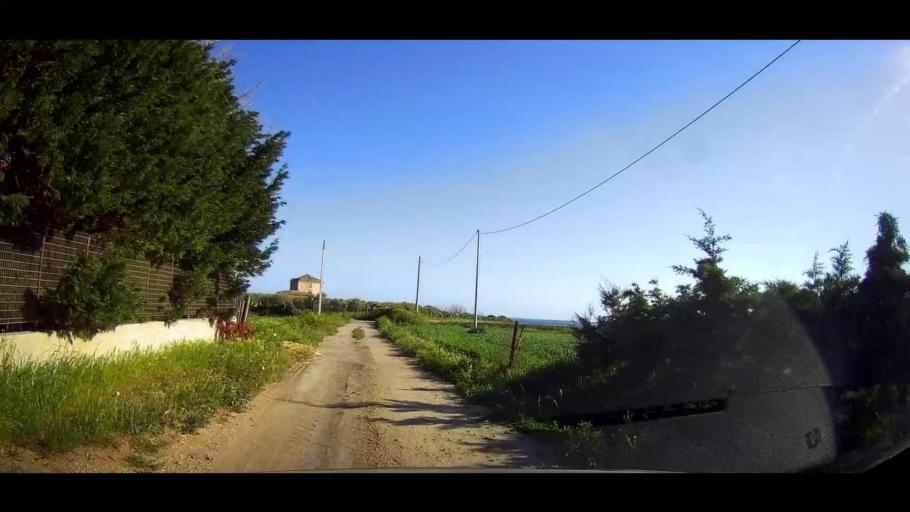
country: IT
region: Calabria
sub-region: Provincia di Crotone
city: Crotone
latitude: 39.0202
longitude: 17.1863
